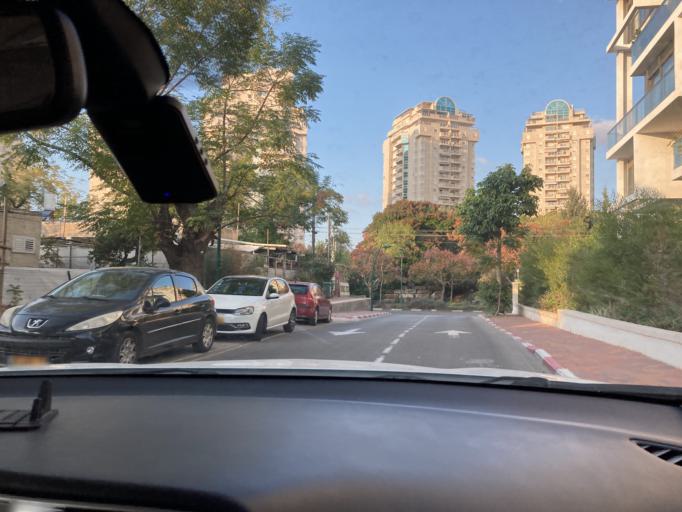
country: IL
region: Tel Aviv
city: Ramat HaSharon
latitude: 32.1496
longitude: 34.8452
